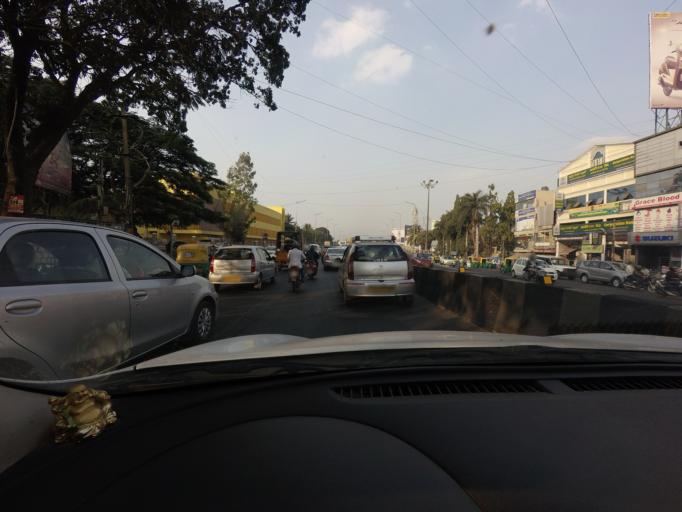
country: IN
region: Karnataka
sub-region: Bangalore Urban
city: Bangalore
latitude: 13.0228
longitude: 77.5845
